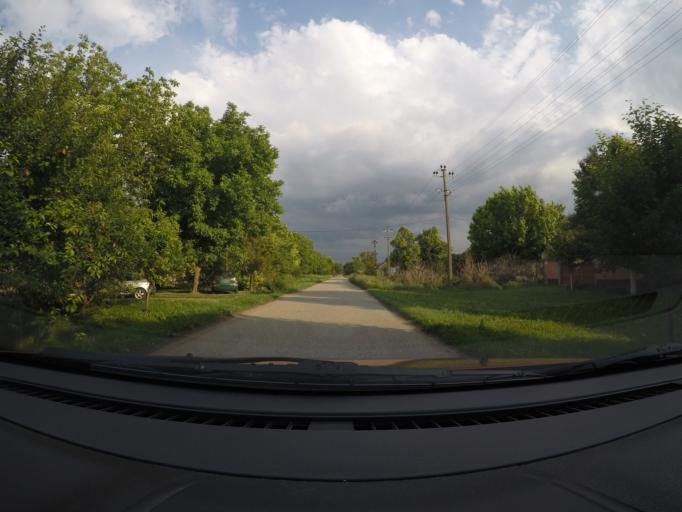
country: RS
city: Debeljaca
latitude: 45.0668
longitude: 20.5999
